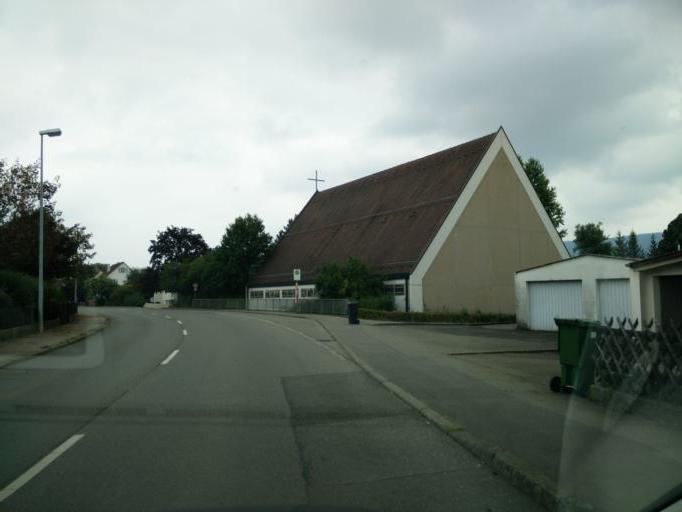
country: DE
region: Baden-Wuerttemberg
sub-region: Tuebingen Region
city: Gomaringen
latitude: 48.4510
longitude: 9.0916
